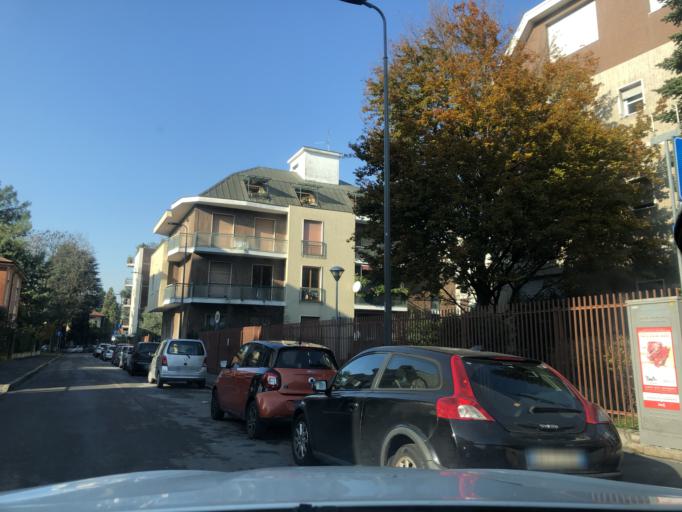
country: IT
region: Lombardy
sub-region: Citta metropolitana di Milano
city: Milano
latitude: 45.4986
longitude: 9.2030
